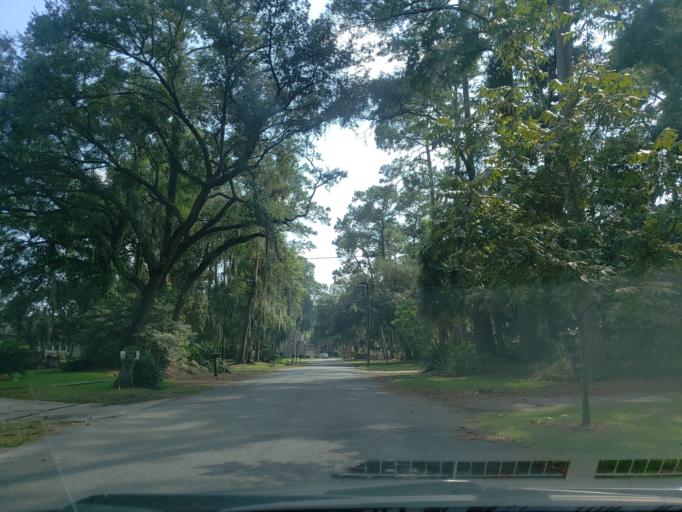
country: US
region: Georgia
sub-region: Chatham County
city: Montgomery
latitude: 31.9297
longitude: -81.0959
